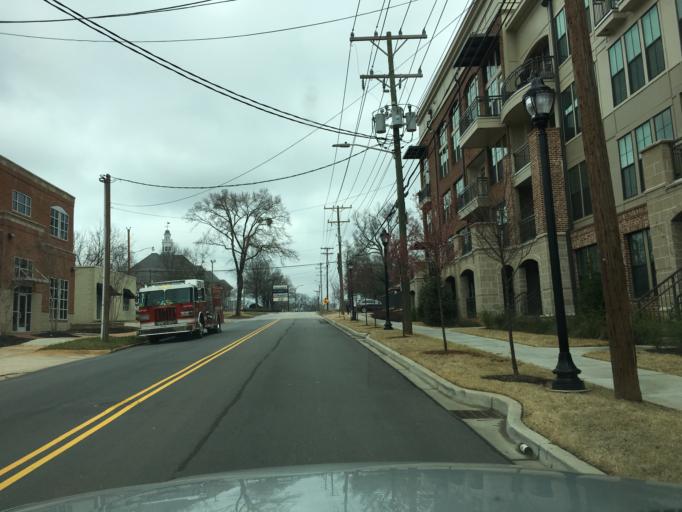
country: US
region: South Carolina
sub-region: Greenville County
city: Greenville
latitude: 34.8497
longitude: -82.4062
